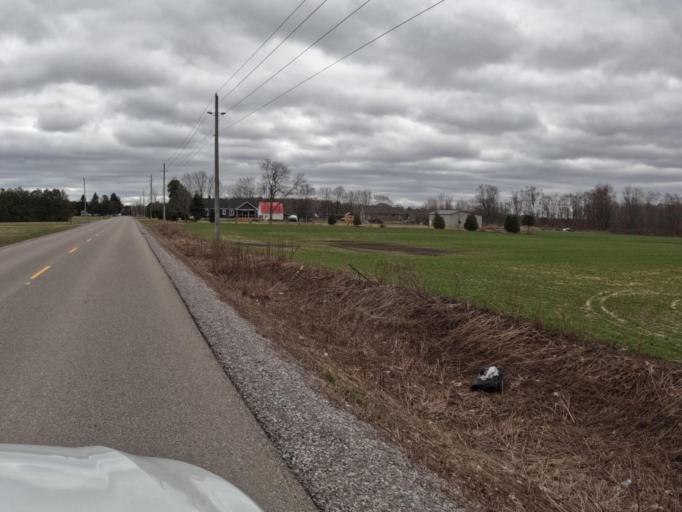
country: CA
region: Ontario
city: Norfolk County
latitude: 42.8721
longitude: -80.4091
